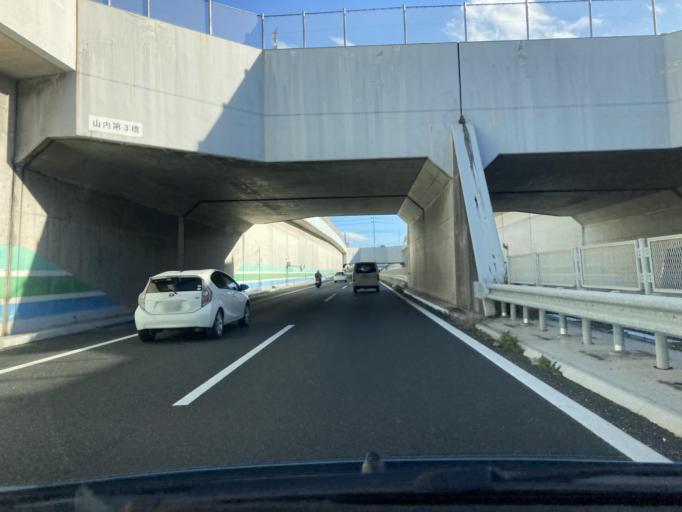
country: JP
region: Okinawa
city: Okinawa
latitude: 26.3285
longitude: 127.7854
